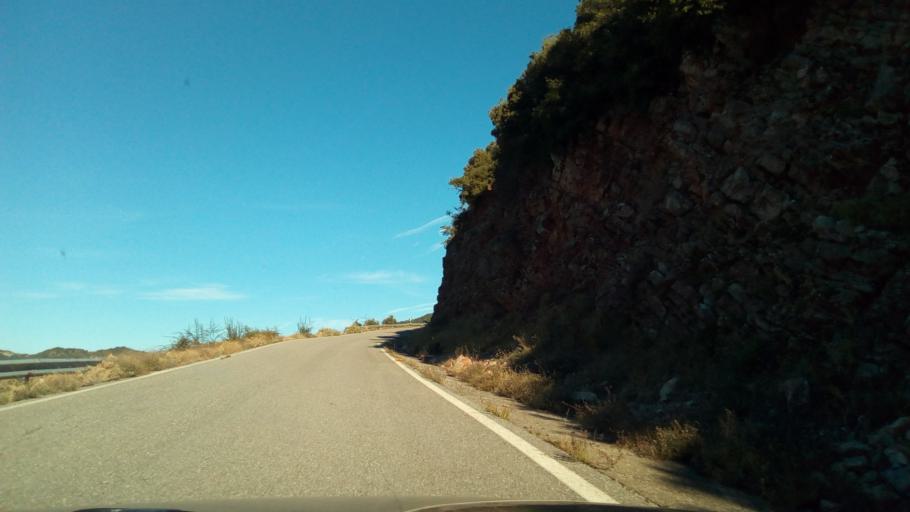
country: GR
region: West Greece
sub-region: Nomos Aitolias kai Akarnanias
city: Nafpaktos
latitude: 38.4874
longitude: 21.8581
